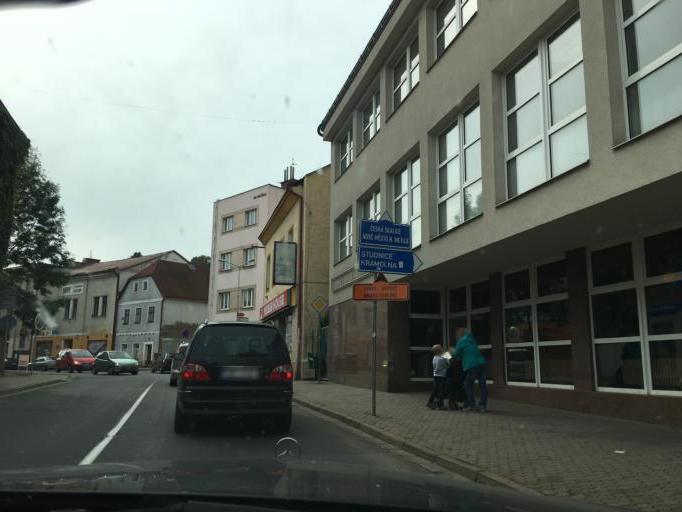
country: CZ
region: Kralovehradecky
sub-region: Okres Nachod
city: Nachod
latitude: 50.4157
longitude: 16.1610
